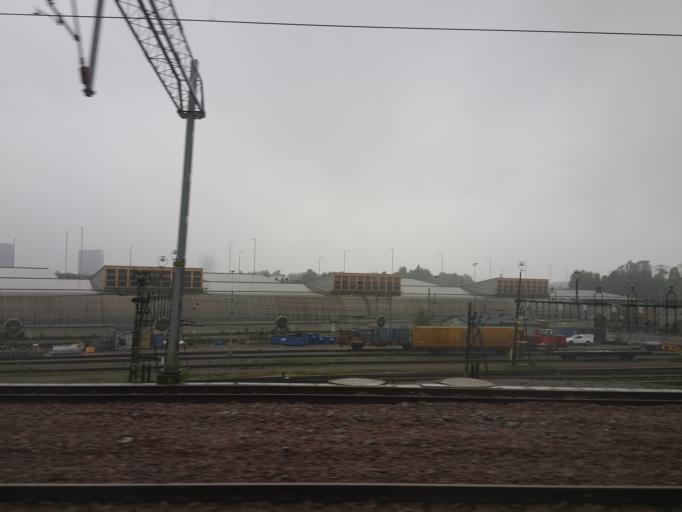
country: SE
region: Stockholm
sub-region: Solna Kommun
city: Solna
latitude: 59.3466
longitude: 18.0204
